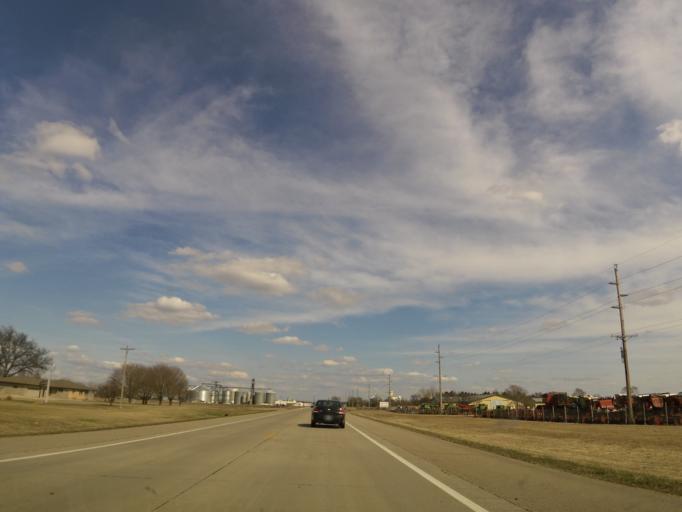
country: US
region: Minnesota
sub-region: Lac qui Parle County
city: Dawson
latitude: 44.9357
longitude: -96.0789
